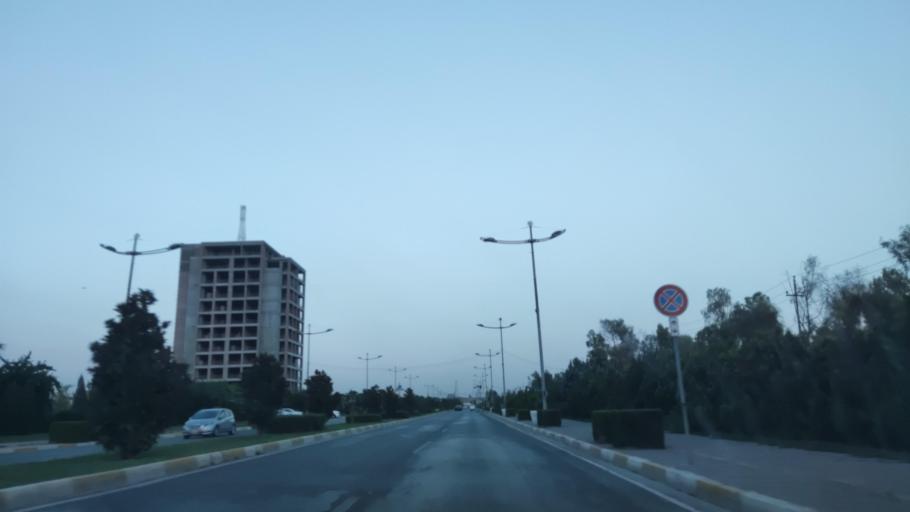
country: IQ
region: Arbil
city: Erbil
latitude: 36.1986
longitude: 43.9842
